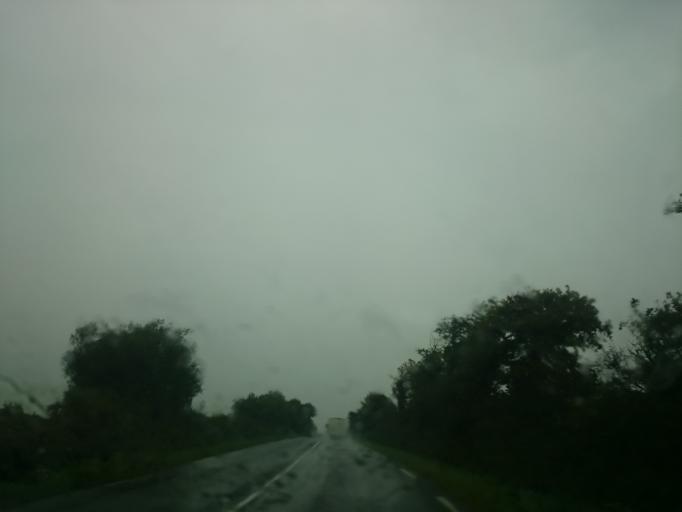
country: FR
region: Brittany
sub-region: Departement du Finistere
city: Gouesnou
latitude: 48.4696
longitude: -4.4440
